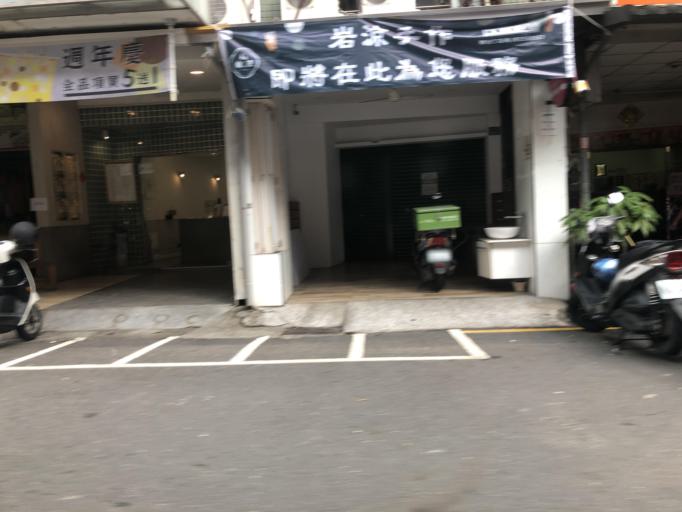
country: TW
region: Kaohsiung
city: Kaohsiung
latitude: 22.7264
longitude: 120.3051
